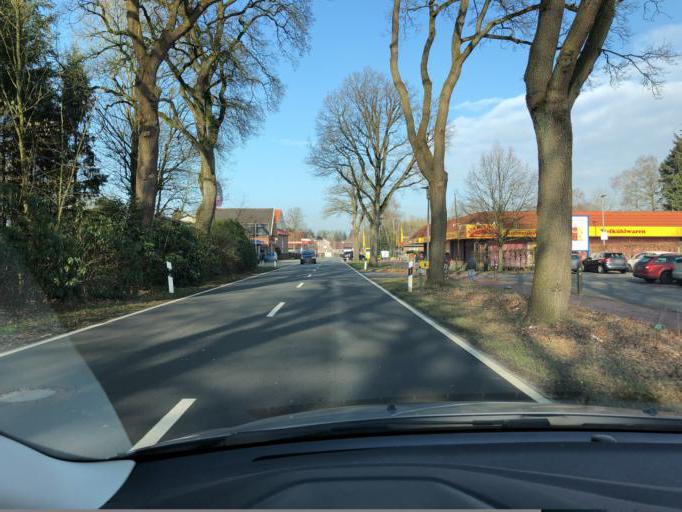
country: DE
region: Lower Saxony
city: Westerstede
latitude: 53.2601
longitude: 7.9185
